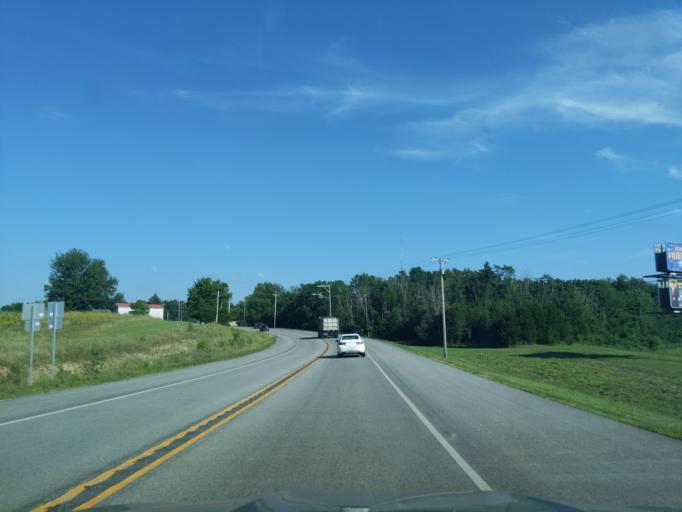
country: US
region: Indiana
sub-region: Ripley County
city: Versailles
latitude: 39.0722
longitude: -85.2694
